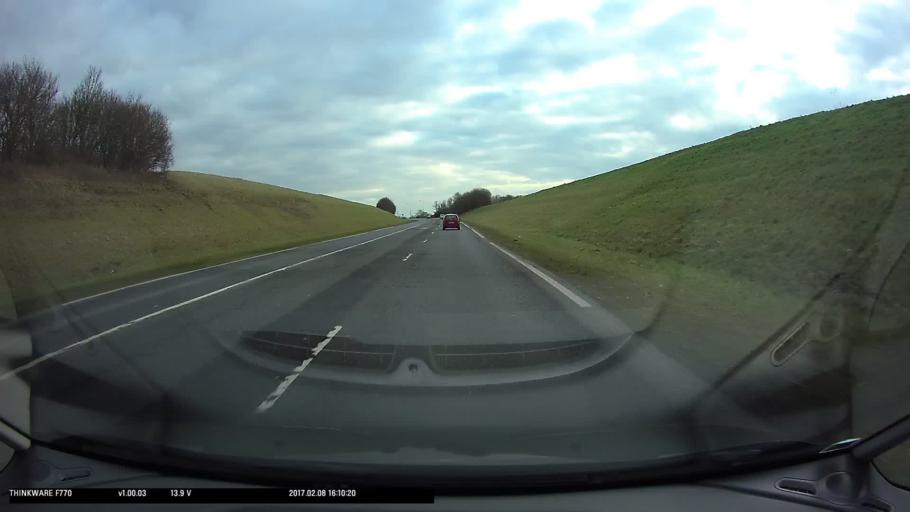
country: FR
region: Ile-de-France
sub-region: Departement du Val-d'Oise
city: Ableiges
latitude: 49.1152
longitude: 2.0299
